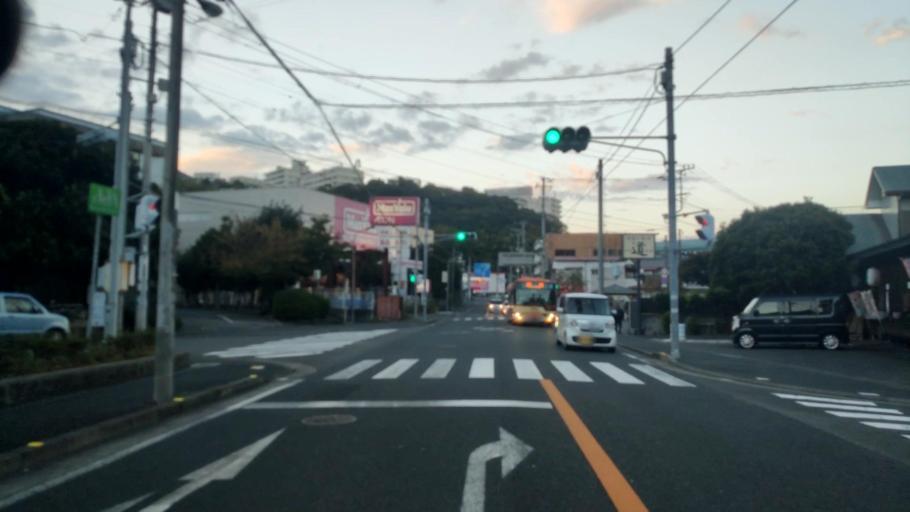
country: JP
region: Shizuoka
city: Ito
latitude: 34.9612
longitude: 139.0913
